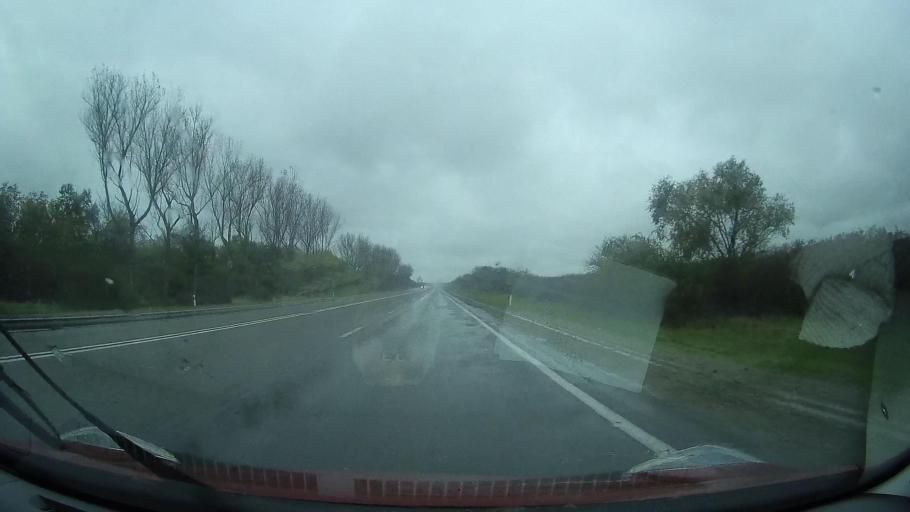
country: RU
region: Stavropol'skiy
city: Nevinnomyssk
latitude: 44.6304
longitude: 42.0300
